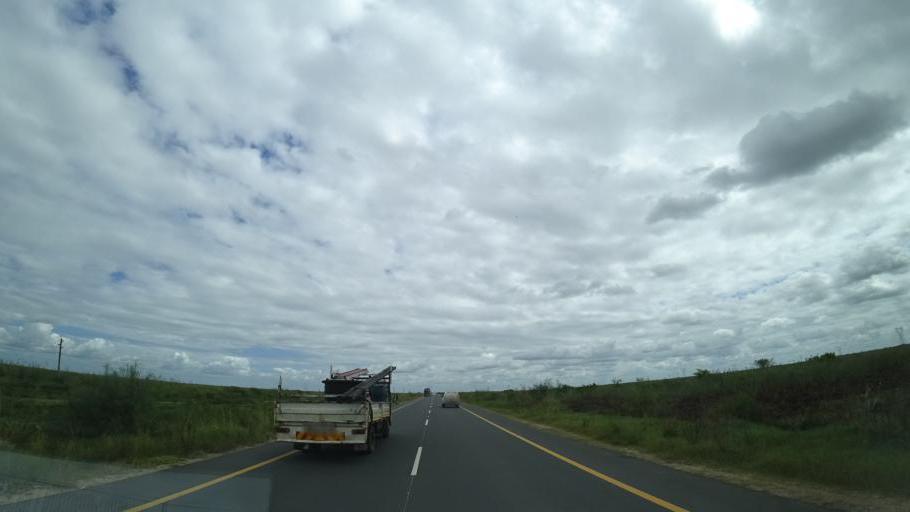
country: MZ
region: Sofala
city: Dondo
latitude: -19.4899
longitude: 34.5842
